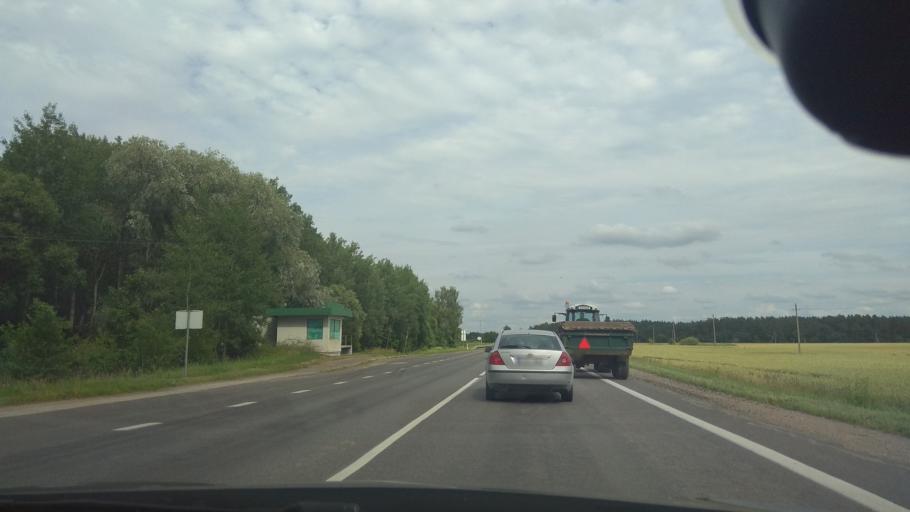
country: LT
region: Panevezys
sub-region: Panevezys City
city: Panevezys
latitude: 55.7343
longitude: 24.2441
